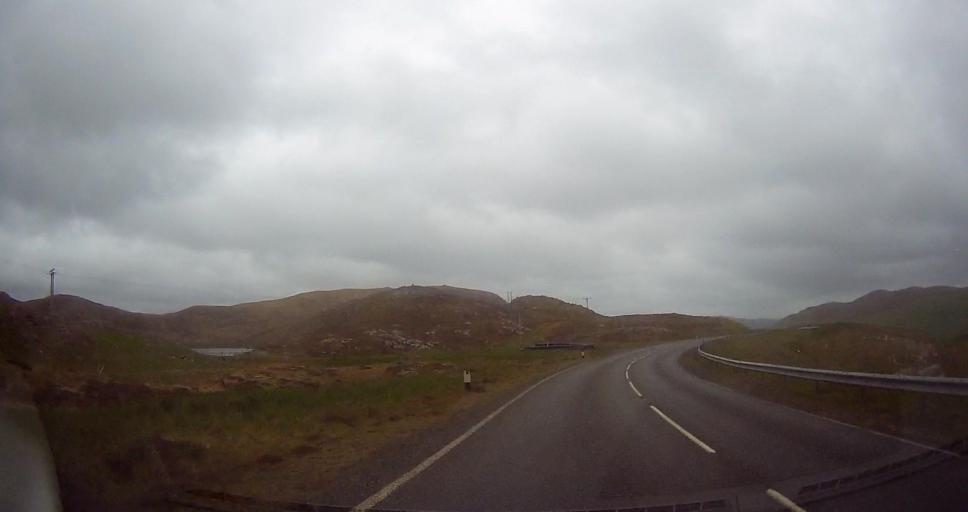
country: GB
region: Scotland
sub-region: Shetland Islands
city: Lerwick
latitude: 60.4174
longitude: -1.3930
